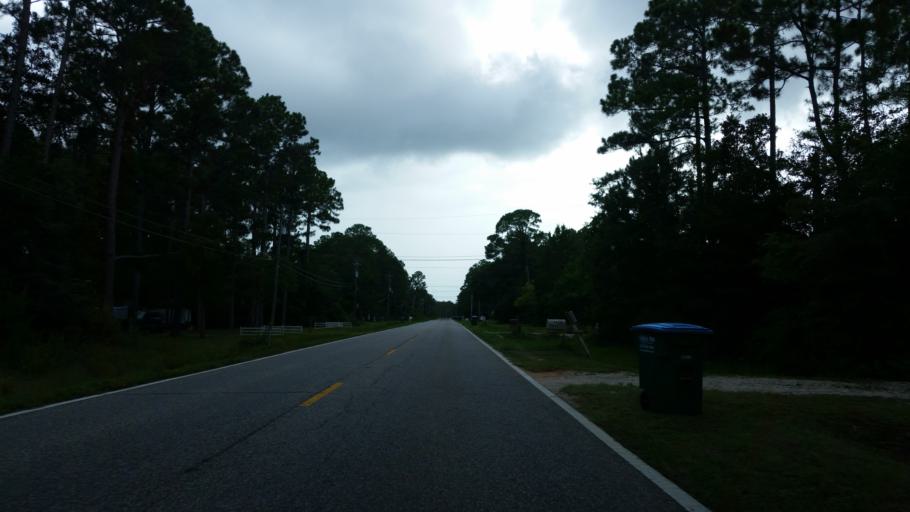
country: US
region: Florida
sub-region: Santa Rosa County
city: Holley
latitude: 30.4399
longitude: -86.9533
